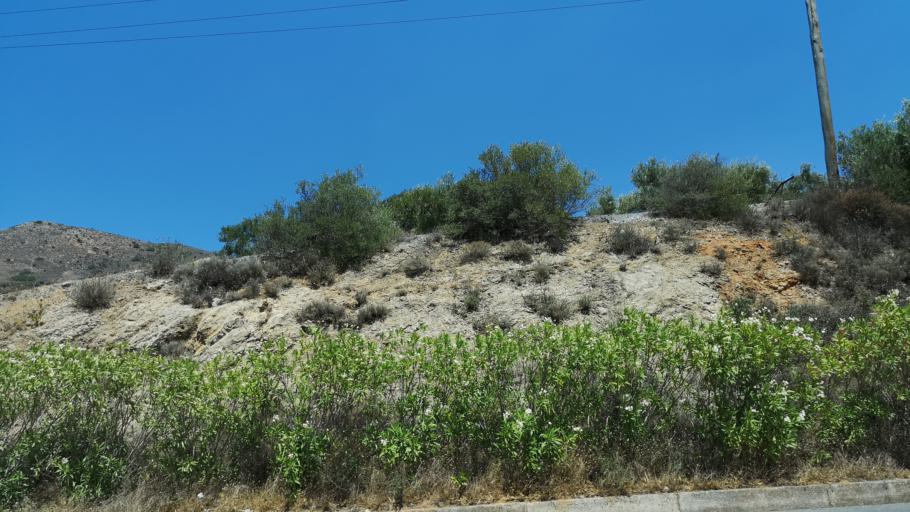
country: GR
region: Crete
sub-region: Nomos Lasithiou
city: Neapoli
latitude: 35.2378
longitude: 25.6475
